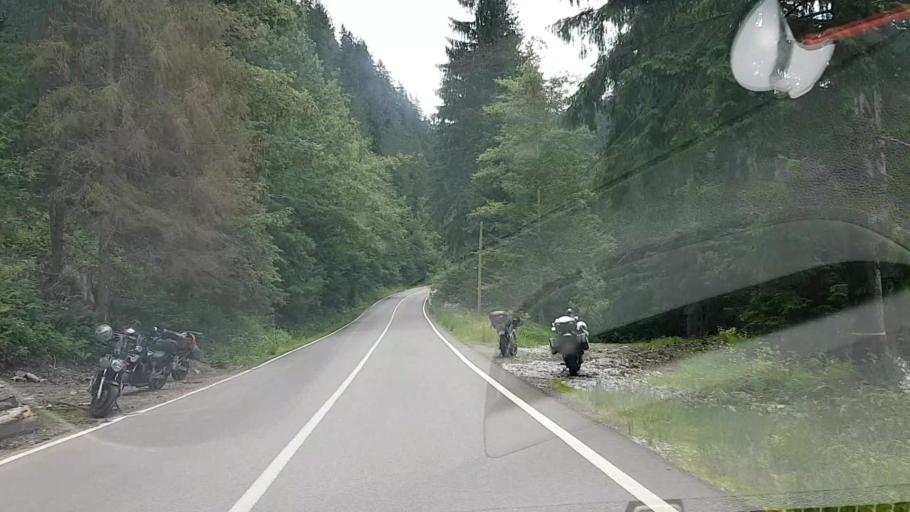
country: RO
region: Suceava
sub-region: Comuna Crucea
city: Crucea
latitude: 47.3648
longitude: 25.5916
